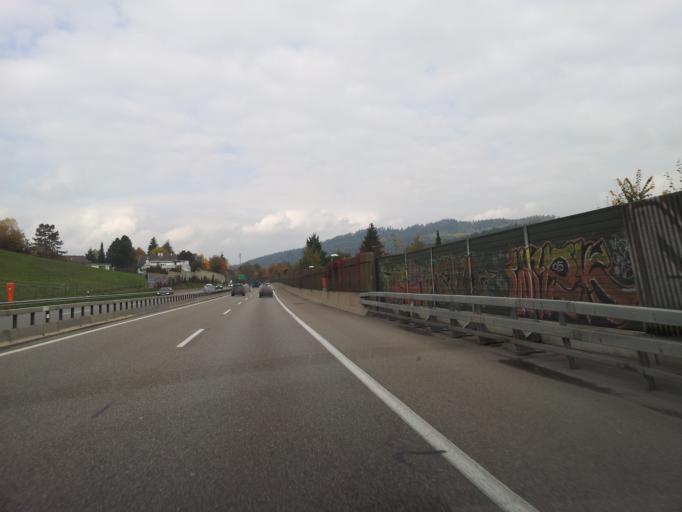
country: CH
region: Bern
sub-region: Bern-Mittelland District
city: Muri
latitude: 46.9285
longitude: 7.5009
